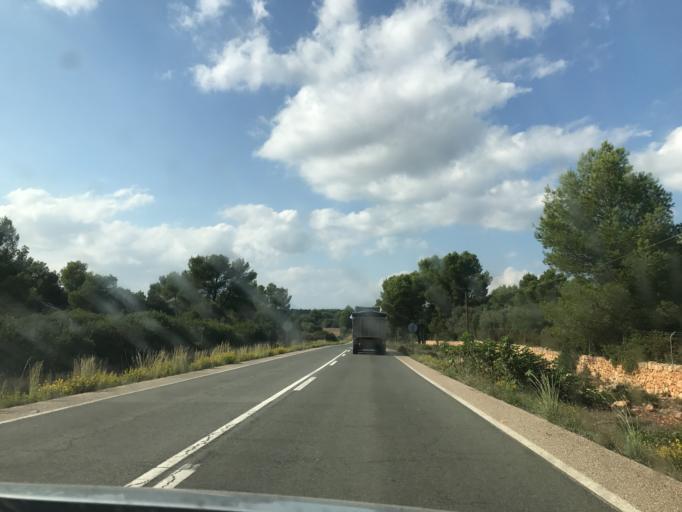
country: ES
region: Balearic Islands
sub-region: Illes Balears
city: Santa Margalida
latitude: 39.7249
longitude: 3.2073
